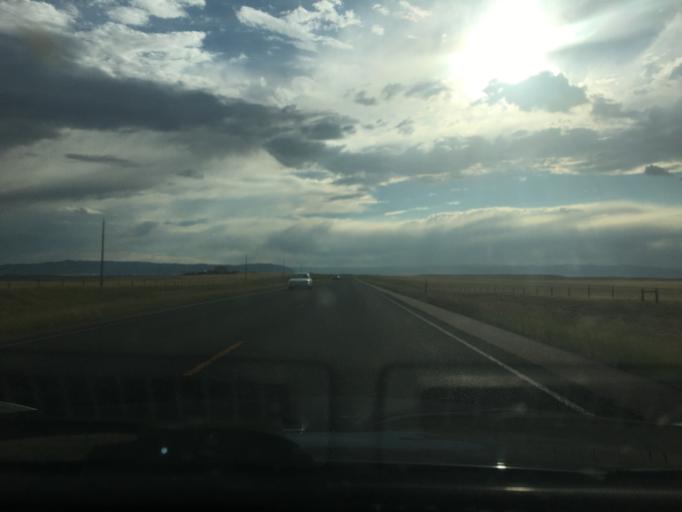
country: US
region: Wyoming
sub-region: Albany County
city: Laramie
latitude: 41.3263
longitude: -105.7271
